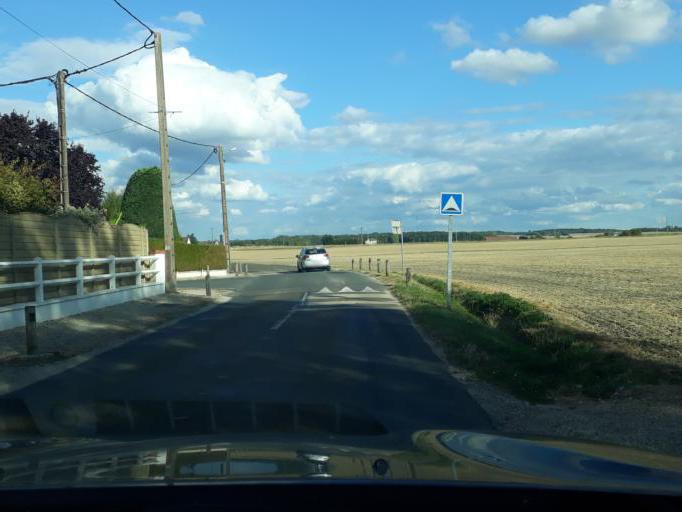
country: FR
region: Centre
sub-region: Departement du Loiret
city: Rebrechien
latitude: 47.9848
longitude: 2.0378
